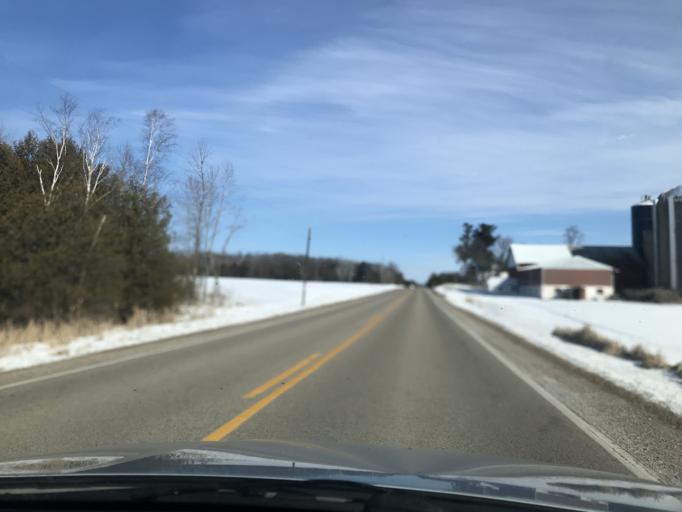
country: US
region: Wisconsin
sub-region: Oconto County
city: Oconto Falls
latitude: 44.9131
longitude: -88.1551
